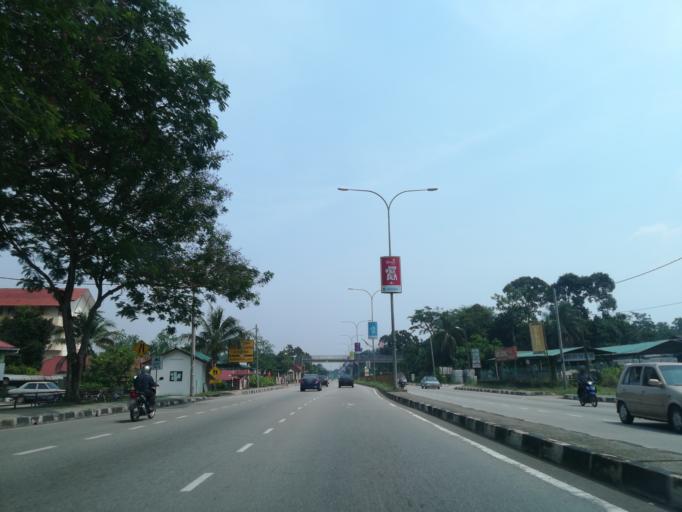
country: MY
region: Kedah
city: Kulim
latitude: 5.4143
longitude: 100.5414
